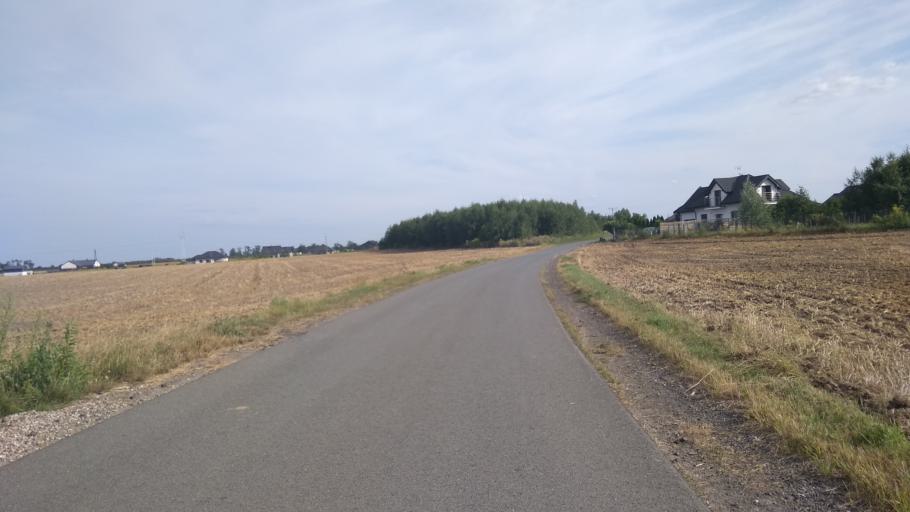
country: PL
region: Kujawsko-Pomorskie
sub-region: Powiat bydgoski
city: Osielsko
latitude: 53.2213
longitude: 18.1451
